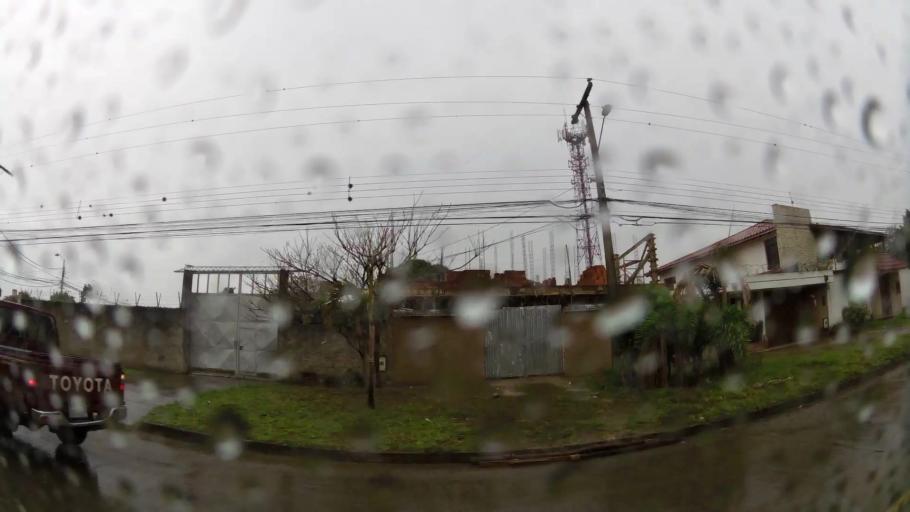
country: BO
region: Santa Cruz
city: Santa Cruz de la Sierra
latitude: -17.8049
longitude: -63.1618
